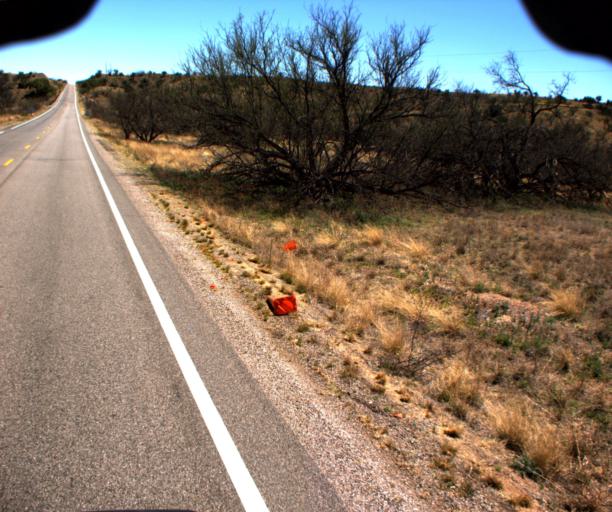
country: US
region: Arizona
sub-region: Pima County
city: Corona de Tucson
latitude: 31.7813
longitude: -110.6928
